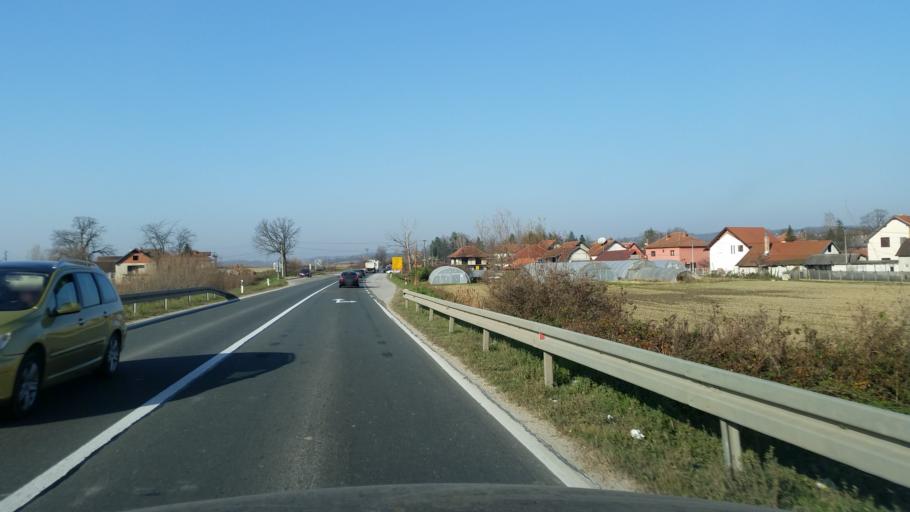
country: RS
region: Central Serbia
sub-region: Kolubarski Okrug
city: Ljig
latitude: 44.2936
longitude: 20.2635
